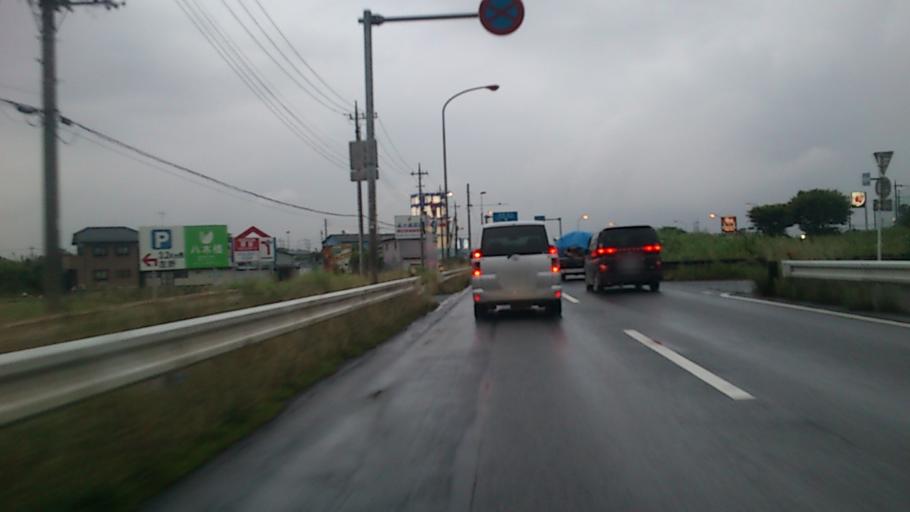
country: JP
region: Saitama
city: Kumagaya
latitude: 36.1527
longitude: 139.4172
